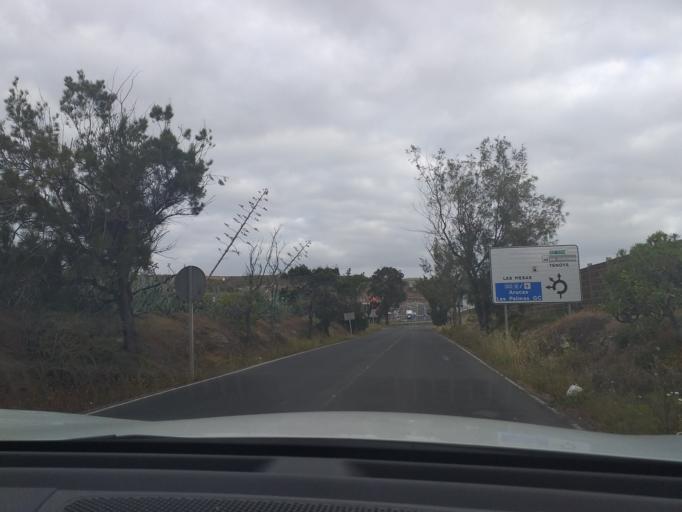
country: ES
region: Canary Islands
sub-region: Provincia de Las Palmas
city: Arucas
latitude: 28.1057
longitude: -15.4887
